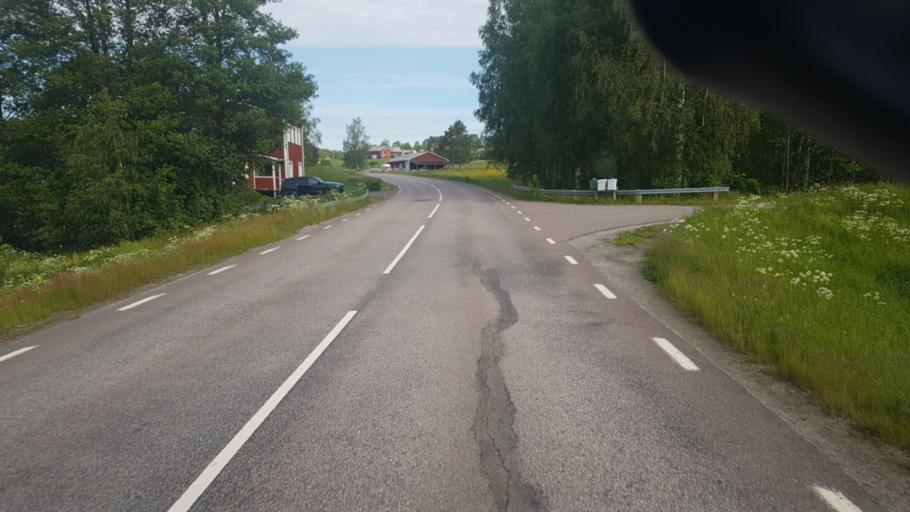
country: SE
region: Vaermland
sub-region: Arvika Kommun
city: Arvika
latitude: 59.7917
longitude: 12.6172
